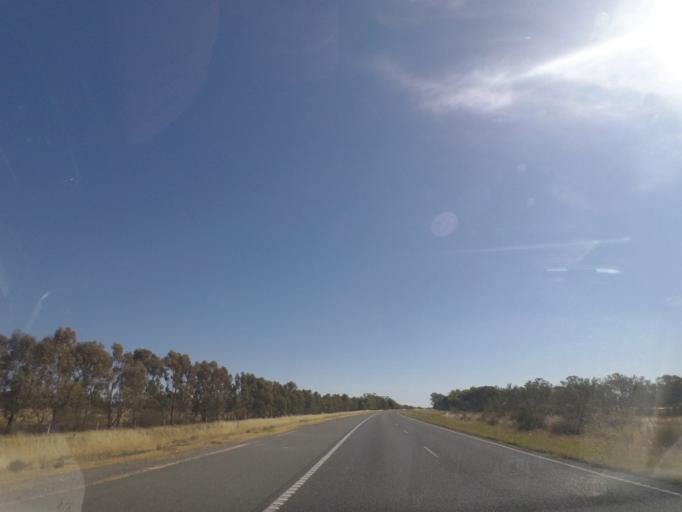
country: AU
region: Victoria
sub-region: Greater Shepparton
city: Shepparton
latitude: -36.6596
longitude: 145.2808
